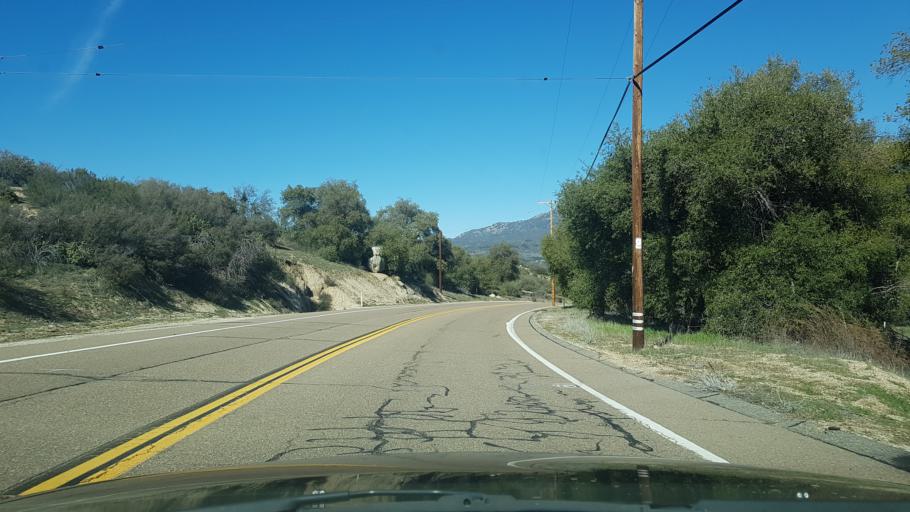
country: US
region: California
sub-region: San Diego County
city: Julian
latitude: 33.2109
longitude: -116.6031
